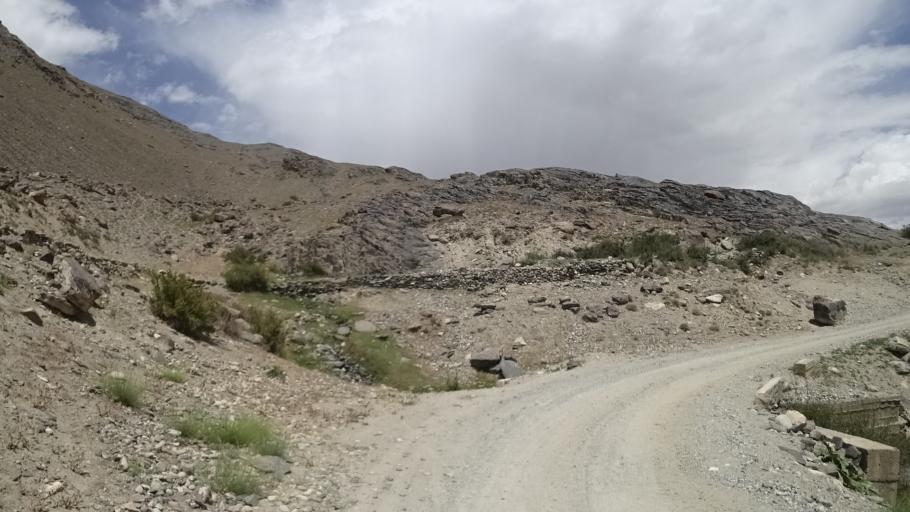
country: AF
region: Badakhshan
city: Khandud
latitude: 37.0956
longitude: 72.7082
